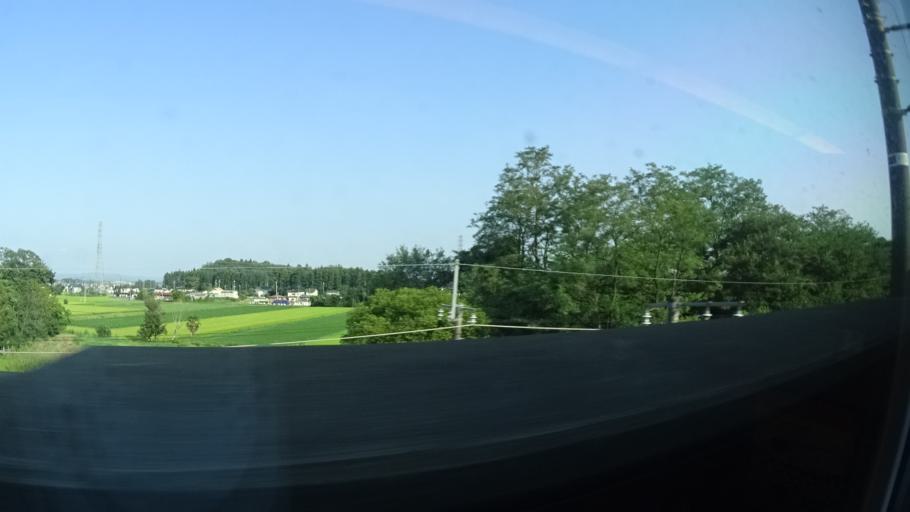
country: JP
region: Tochigi
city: Otawara
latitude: 36.8693
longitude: 139.9760
